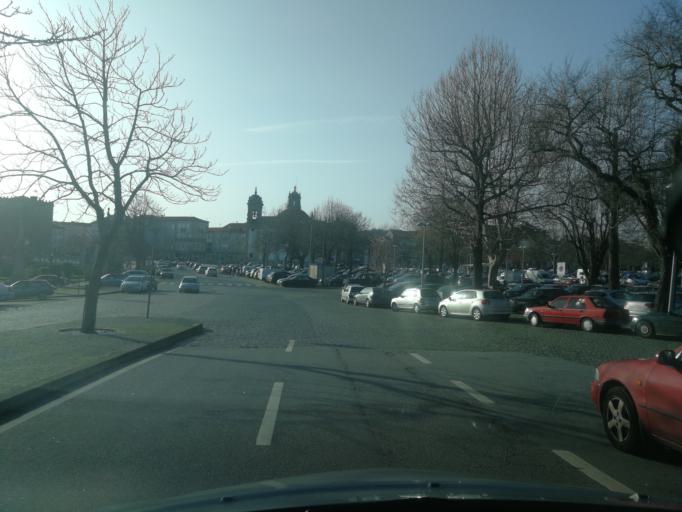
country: PT
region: Braga
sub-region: Barcelos
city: Barcelos
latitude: 41.5318
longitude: -8.6170
